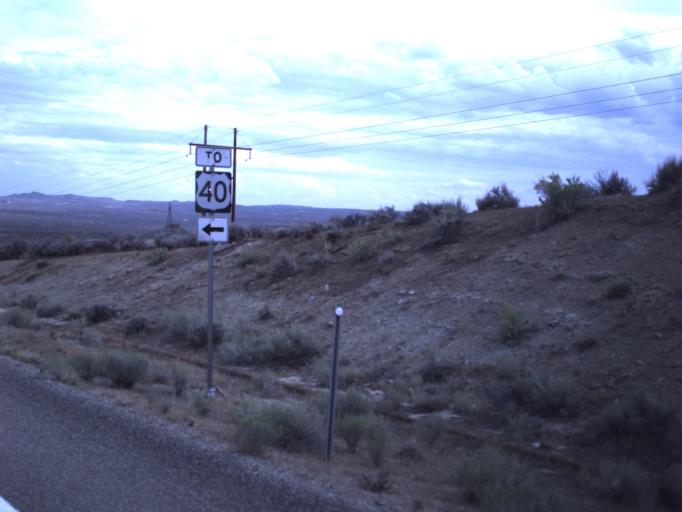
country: US
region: Colorado
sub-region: Rio Blanco County
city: Rangely
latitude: 40.0778
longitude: -109.2101
